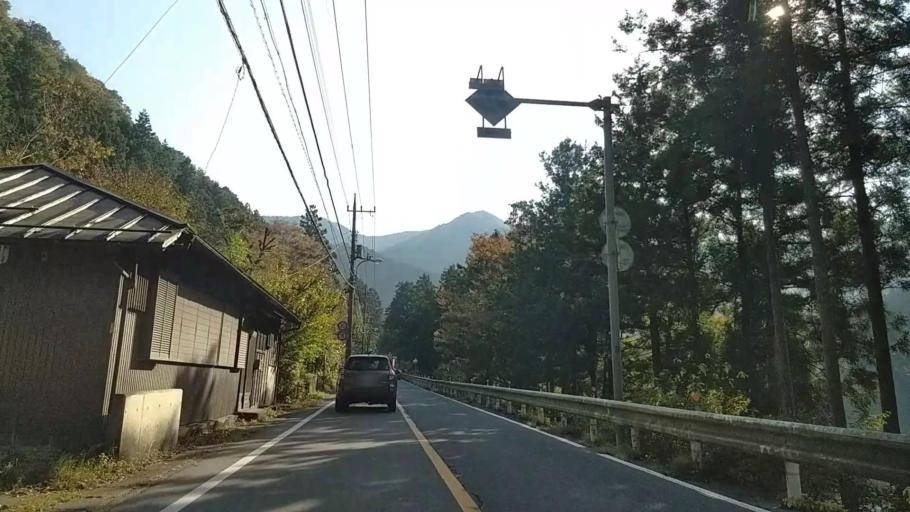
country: JP
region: Tokyo
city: Ome
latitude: 35.8057
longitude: 139.1773
